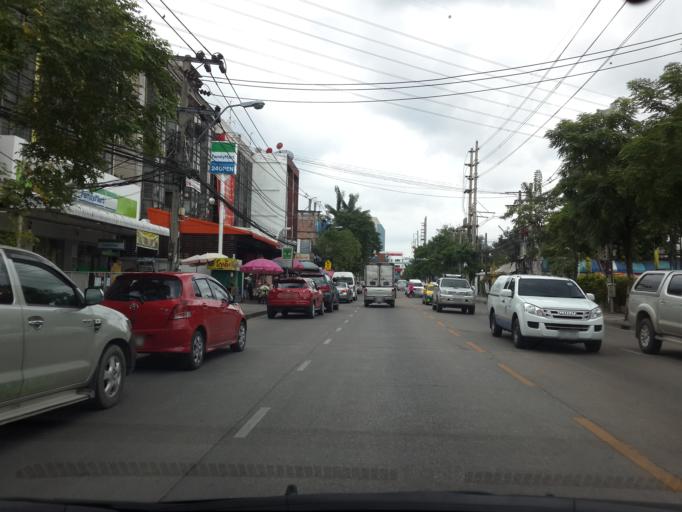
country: TH
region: Bangkok
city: Huai Khwang
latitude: 13.7693
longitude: 100.5899
